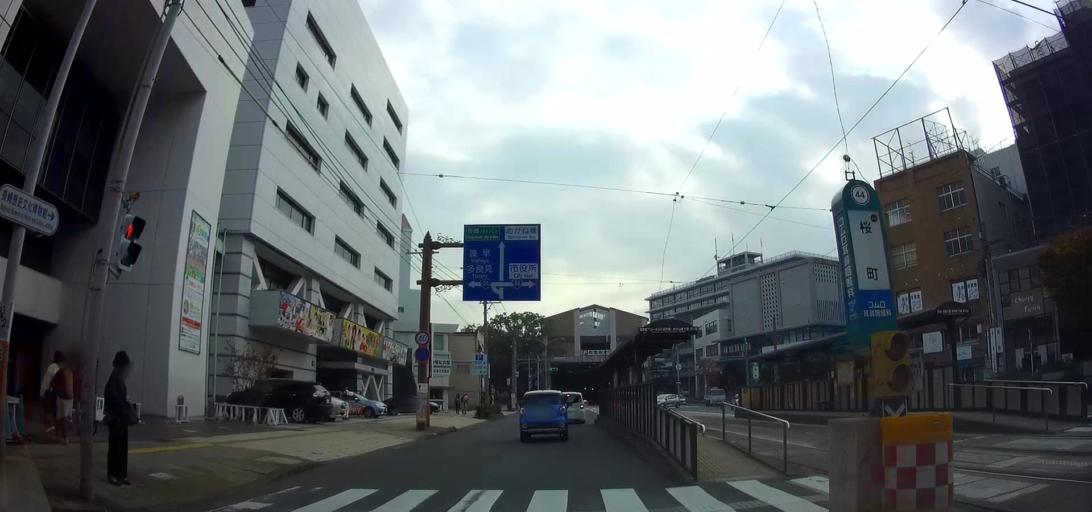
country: JP
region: Nagasaki
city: Nagasaki-shi
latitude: 32.7508
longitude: 129.8761
